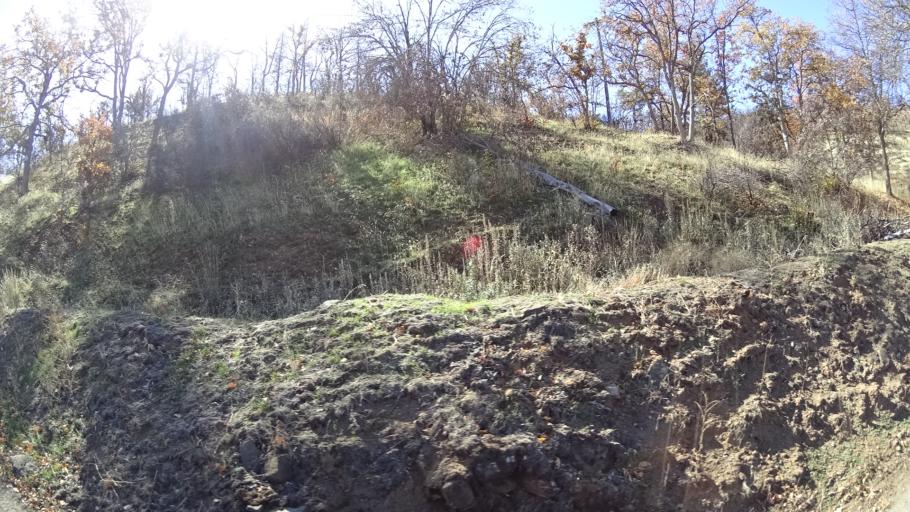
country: US
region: California
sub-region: Siskiyou County
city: Yreka
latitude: 41.9453
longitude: -122.5982
